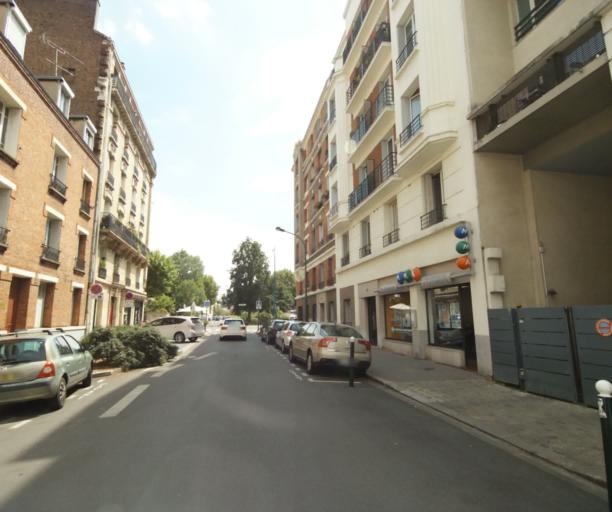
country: FR
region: Ile-de-France
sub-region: Departement des Hauts-de-Seine
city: Asnieres-sur-Seine
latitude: 48.9141
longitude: 2.2872
